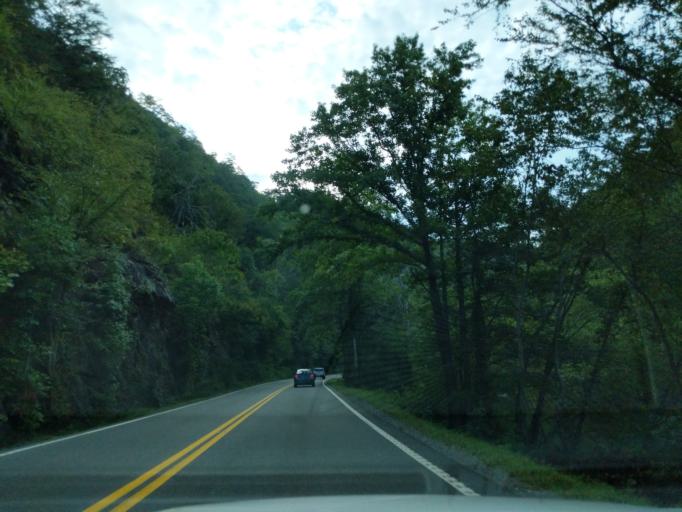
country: US
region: Tennessee
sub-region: Polk County
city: Benton
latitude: 35.0839
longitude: -84.5135
